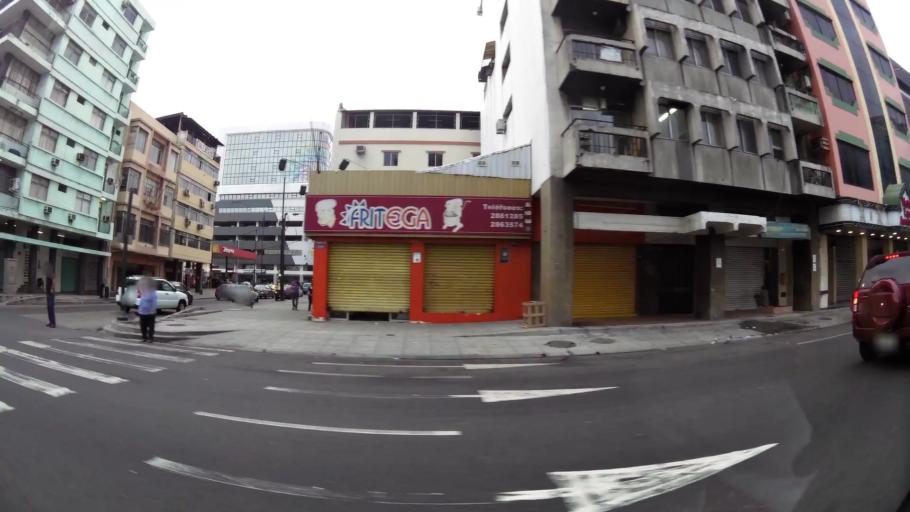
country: EC
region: Guayas
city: Guayaquil
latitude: -2.1887
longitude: -79.8897
